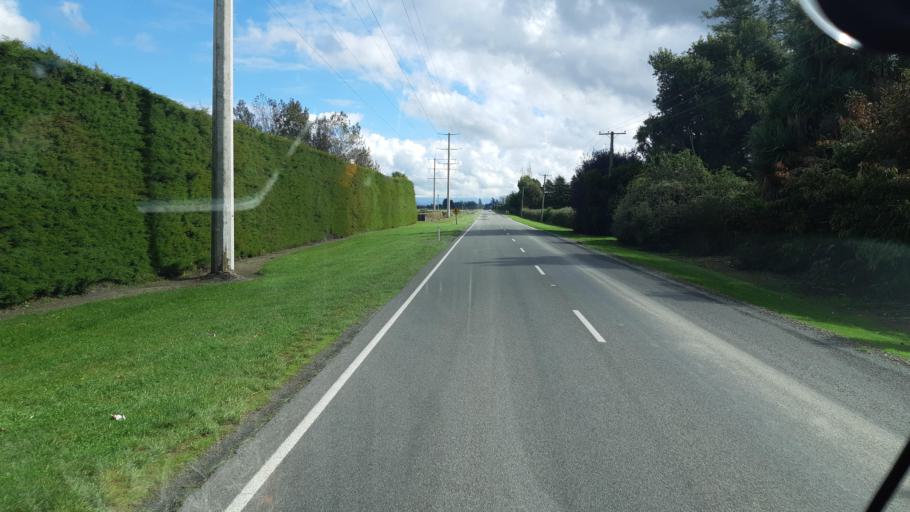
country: NZ
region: Canterbury
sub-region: Selwyn District
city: Darfield
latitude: -43.4736
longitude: 172.2618
